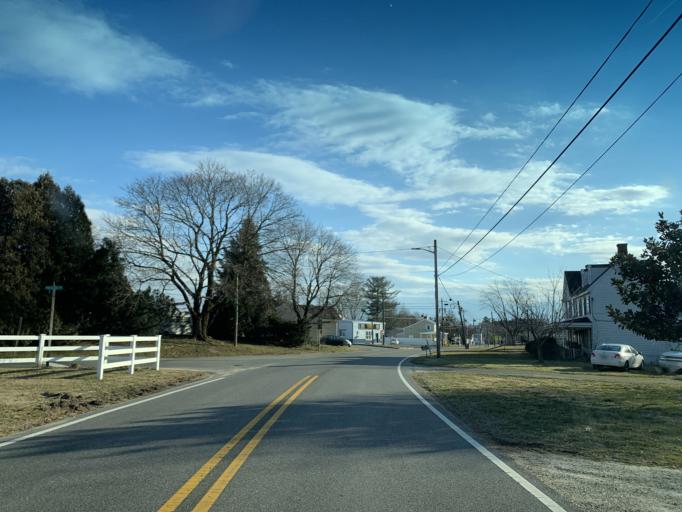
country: US
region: Maryland
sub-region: Queen Anne's County
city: Kingstown
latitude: 39.1495
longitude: -75.9786
